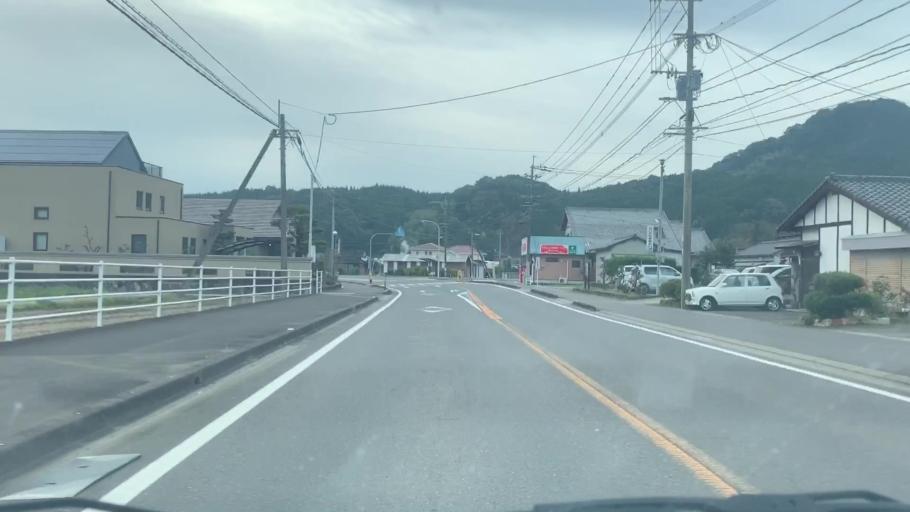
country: JP
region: Saga Prefecture
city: Takeocho-takeo
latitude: 33.1697
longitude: 130.0503
